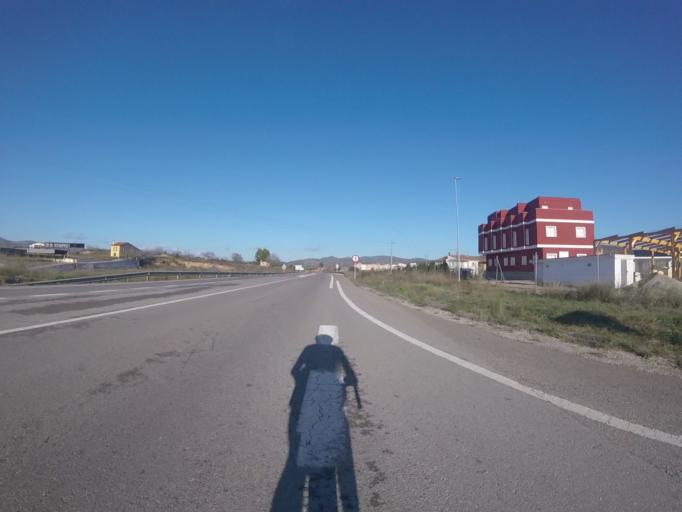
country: ES
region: Valencia
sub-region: Provincia de Castello
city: Cuevas de Vinroma
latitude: 40.3071
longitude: 0.1136
